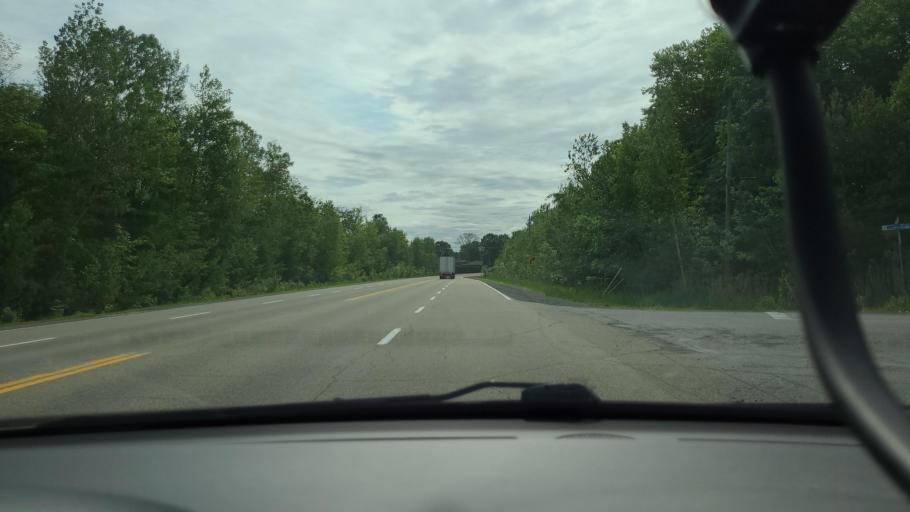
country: CA
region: Quebec
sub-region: Lanaudiere
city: Crabtree
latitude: 45.9708
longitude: -73.4856
